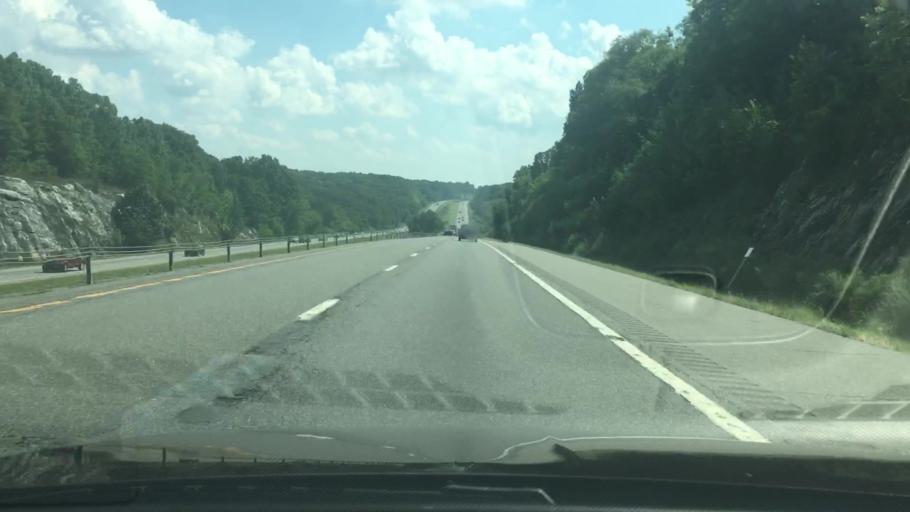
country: US
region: New York
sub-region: Putnam County
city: Lake Carmel
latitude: 41.4549
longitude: -73.6407
